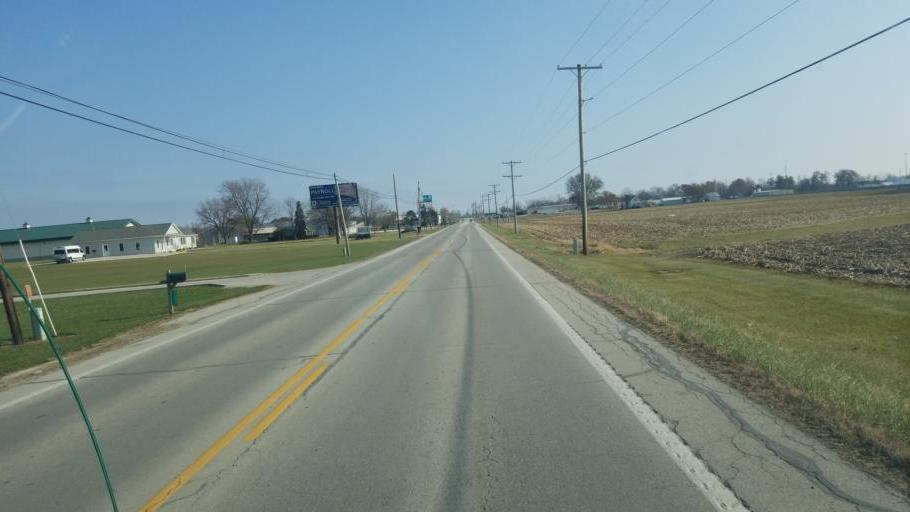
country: US
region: Ohio
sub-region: Mercer County
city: Celina
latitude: 40.5455
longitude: -84.5983
